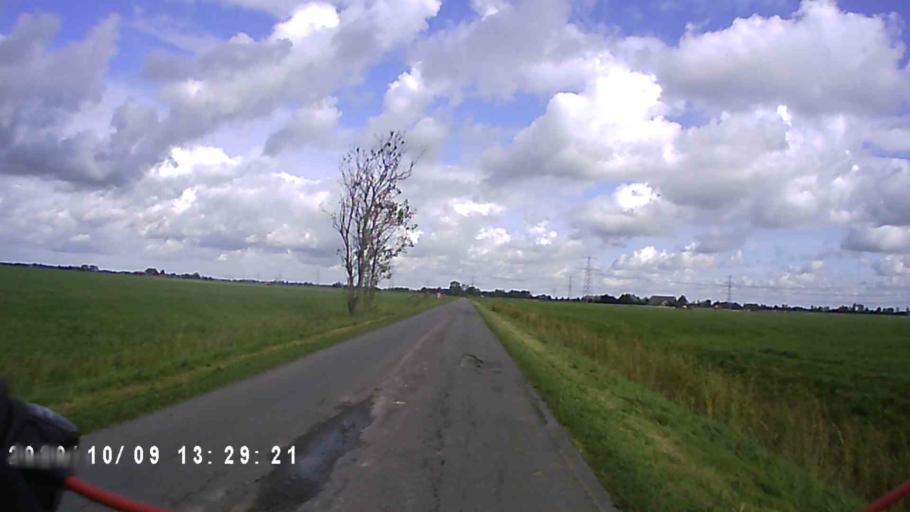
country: NL
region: Groningen
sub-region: Gemeente Zuidhorn
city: Aduard
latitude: 53.2717
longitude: 6.4695
